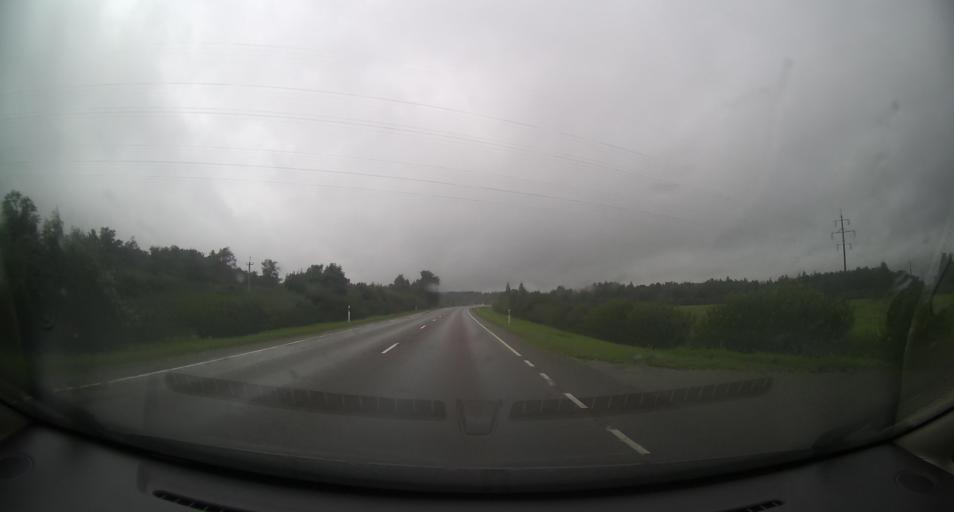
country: EE
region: Laeaene
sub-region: Lihula vald
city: Lihula
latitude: 58.6738
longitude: 23.7726
